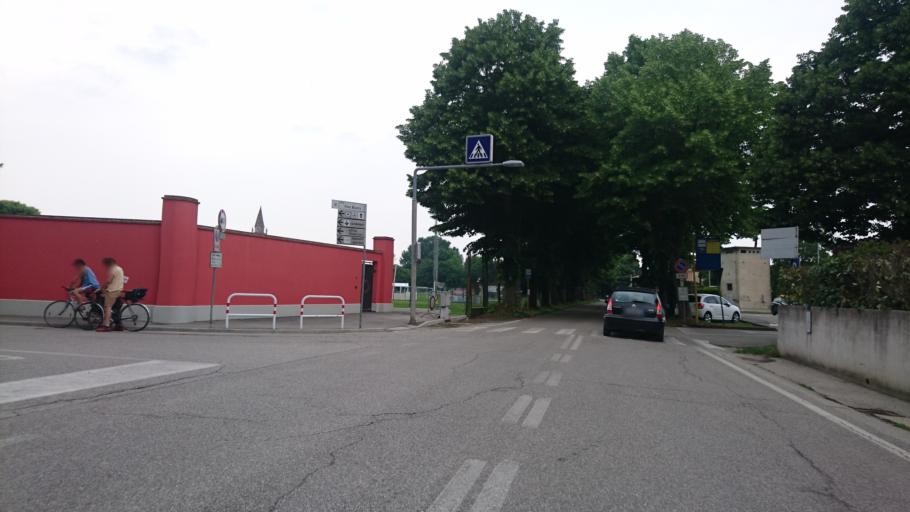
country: IT
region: Veneto
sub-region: Provincia di Rovigo
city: Badia Polesine
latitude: 45.0963
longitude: 11.4949
